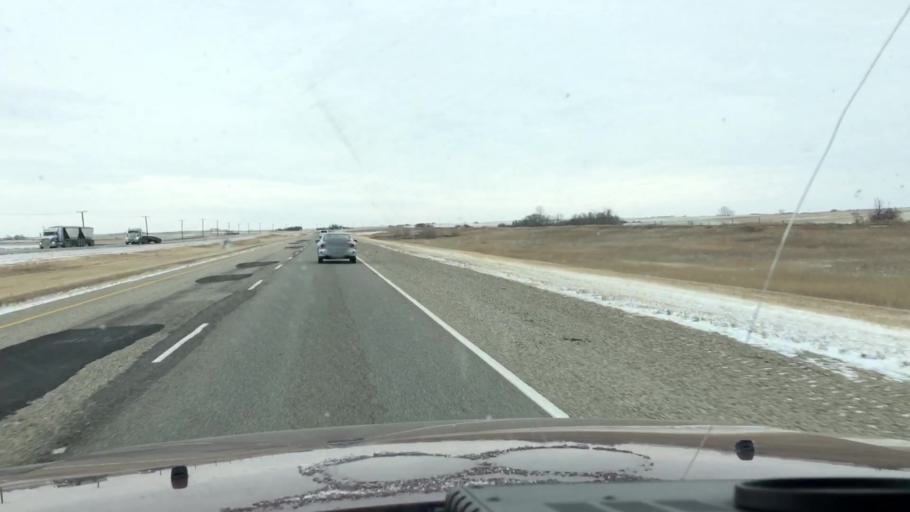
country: CA
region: Saskatchewan
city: Watrous
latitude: 51.4431
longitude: -106.2119
